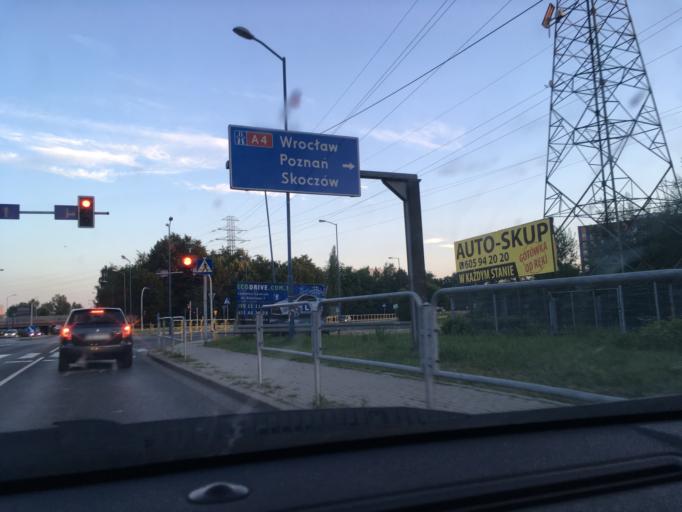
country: PL
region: Silesian Voivodeship
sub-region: Katowice
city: Katowice
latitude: 50.2485
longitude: 19.0260
